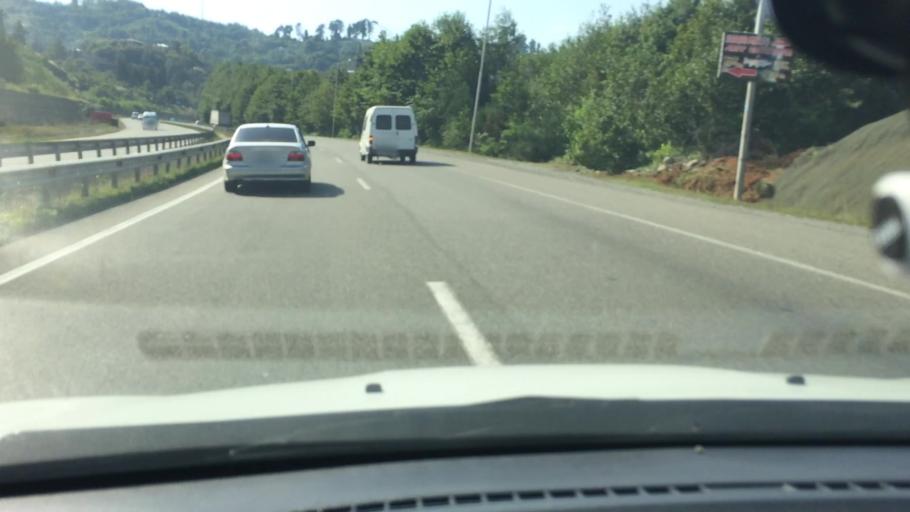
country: GE
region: Ajaria
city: Makhinjauri
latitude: 41.6987
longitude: 41.7283
